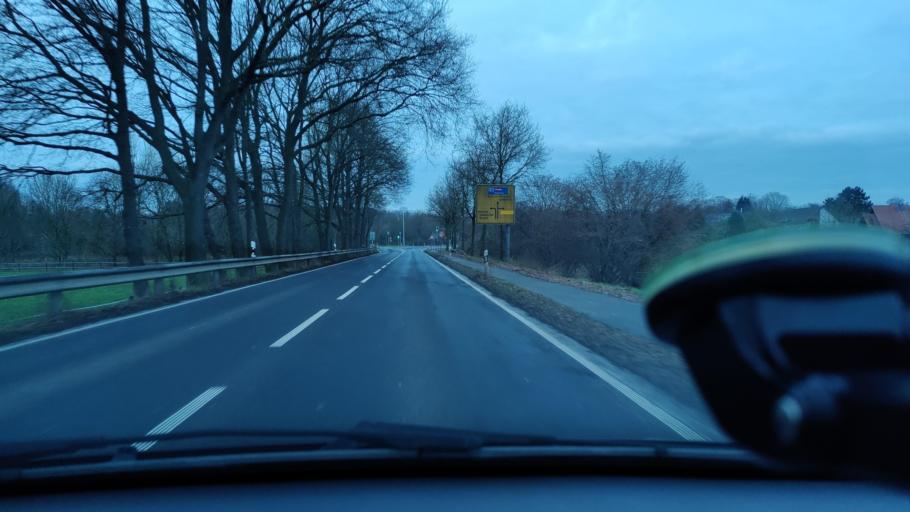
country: DE
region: North Rhine-Westphalia
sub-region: Regierungsbezirk Dusseldorf
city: Nettetal
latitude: 51.2781
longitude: 6.2728
